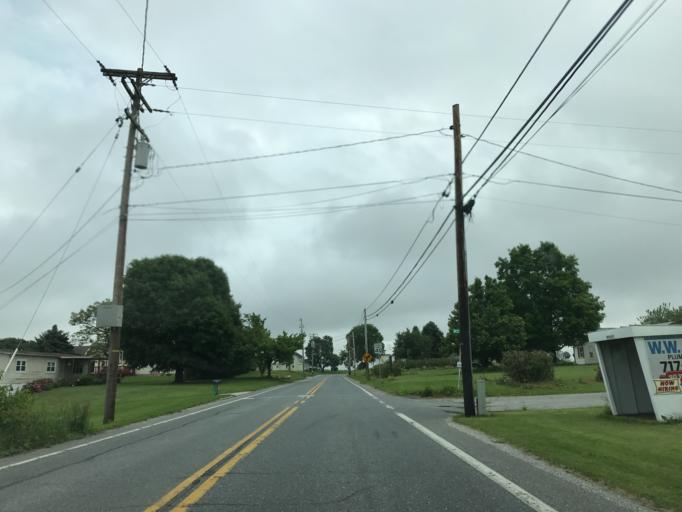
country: US
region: Pennsylvania
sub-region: York County
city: Stewartstown
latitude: 39.8090
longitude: -76.5978
